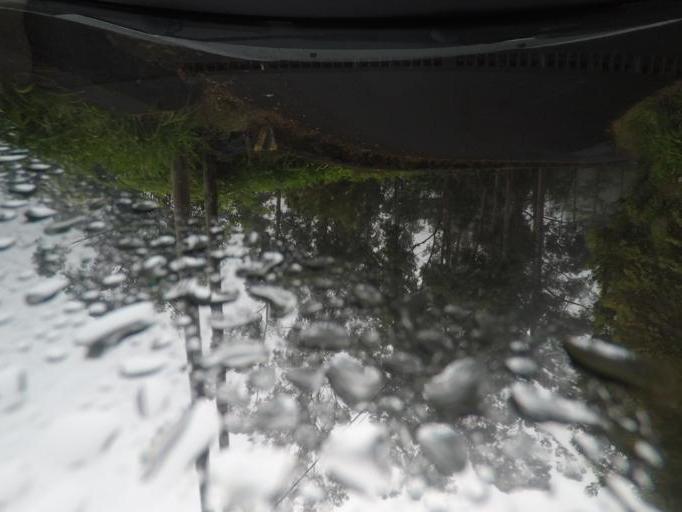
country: PT
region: Madeira
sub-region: Santana
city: Santana
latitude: 32.7562
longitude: -16.8733
